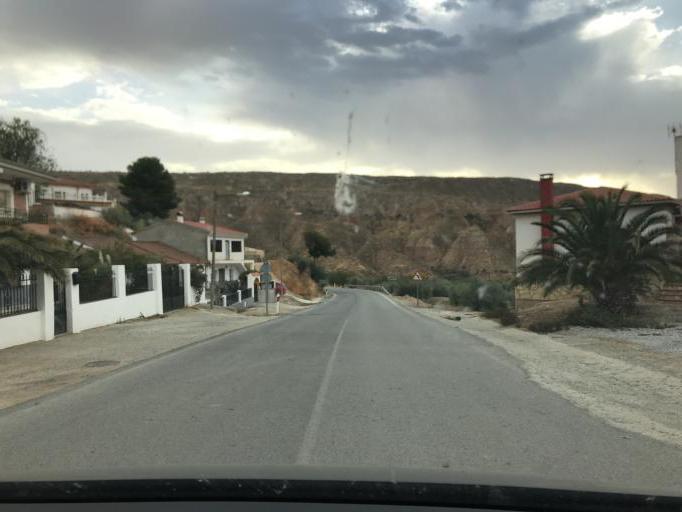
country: ES
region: Andalusia
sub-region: Provincia de Granada
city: Villanueva de las Torres
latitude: 37.4788
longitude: -3.0426
